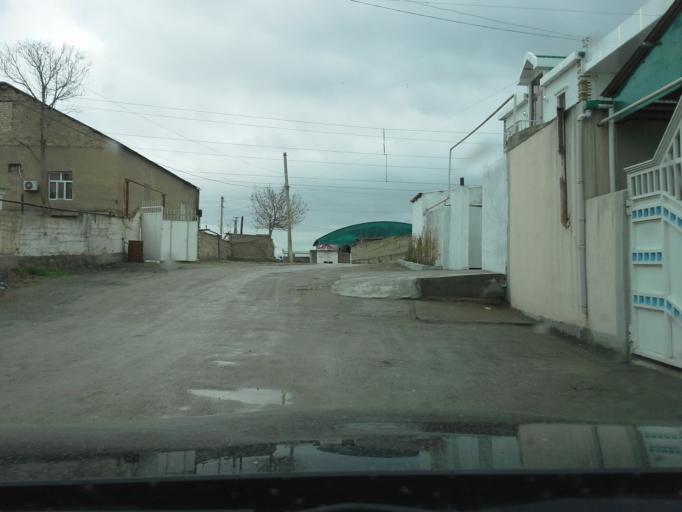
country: TM
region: Ahal
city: Abadan
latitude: 37.9515
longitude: 58.2058
